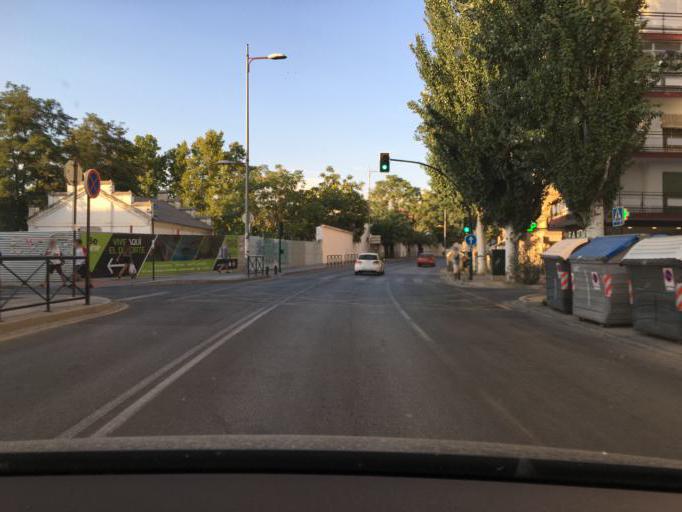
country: ES
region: Andalusia
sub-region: Provincia de Granada
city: Granada
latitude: 37.1903
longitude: -3.6107
